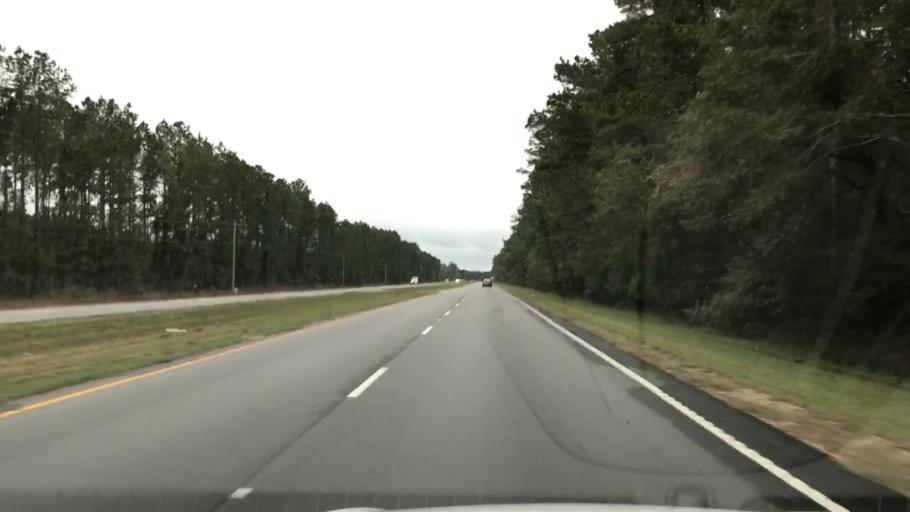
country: US
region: South Carolina
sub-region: Georgetown County
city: Georgetown
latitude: 33.2827
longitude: -79.3499
